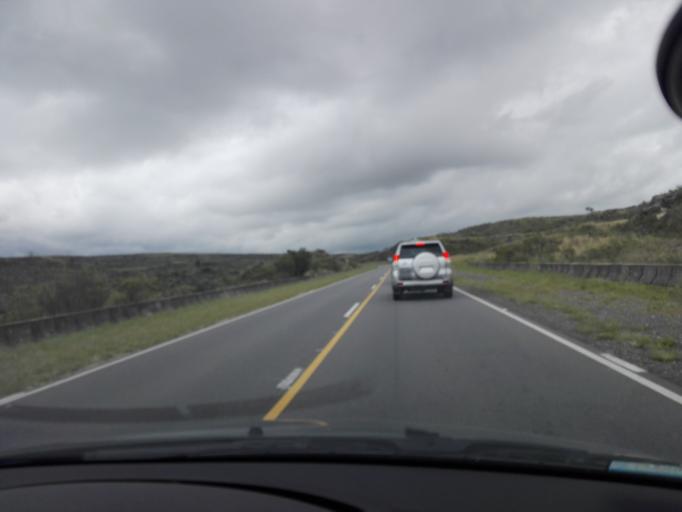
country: AR
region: Cordoba
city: Cuesta Blanca
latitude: -31.5724
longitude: -64.6462
